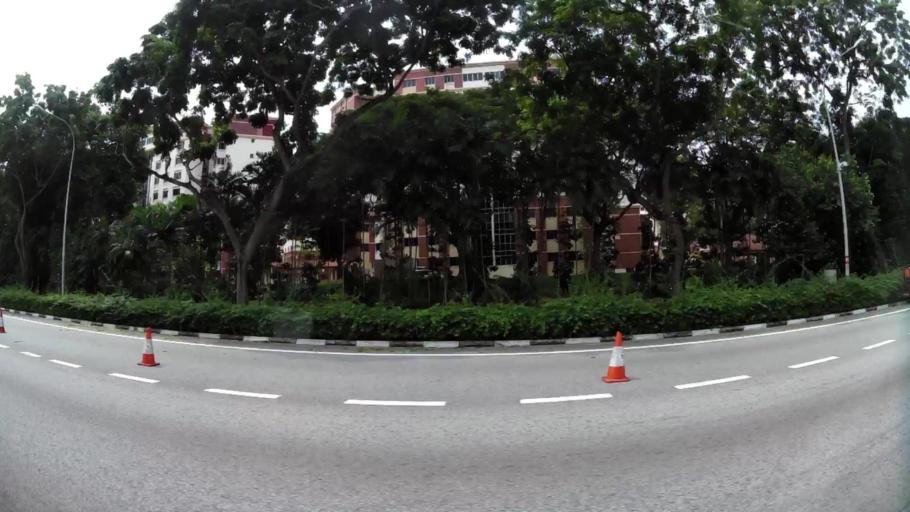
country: SG
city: Singapore
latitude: 1.3630
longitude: 103.9584
